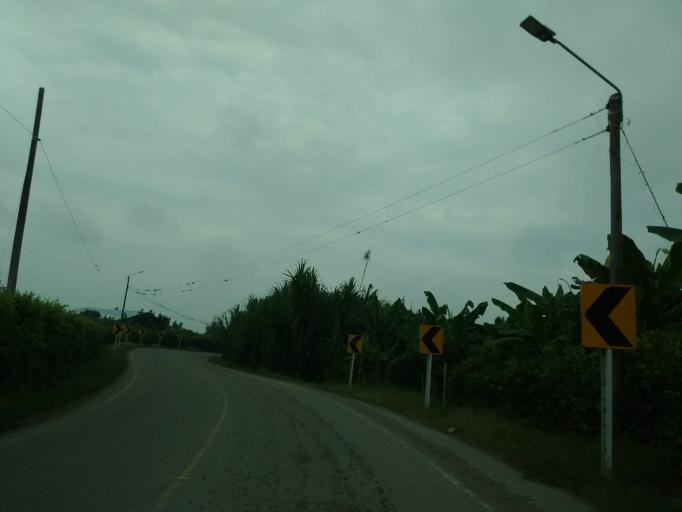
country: CO
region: Cauca
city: Padilla
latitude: 3.2284
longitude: -76.3162
